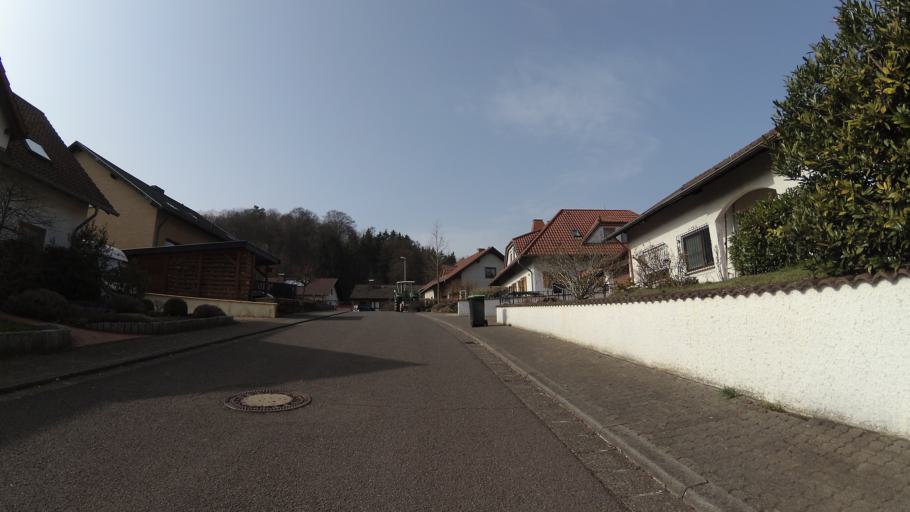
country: DE
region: Saarland
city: Losheim
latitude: 49.4522
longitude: 6.7354
